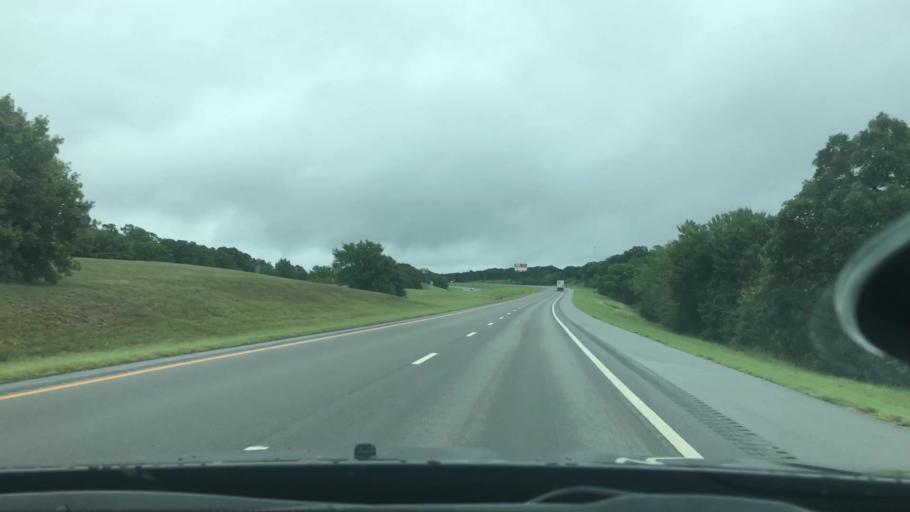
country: US
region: Oklahoma
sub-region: Okmulgee County
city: Henryetta
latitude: 35.4327
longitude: -95.8572
